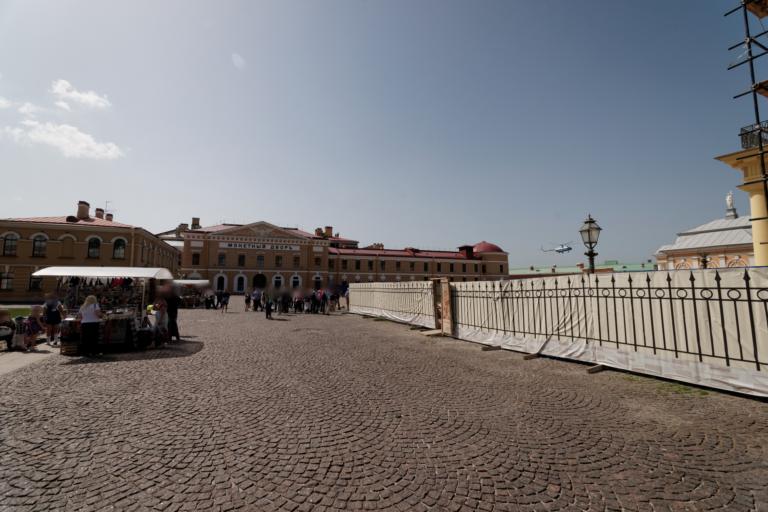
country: RU
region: St.-Petersburg
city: Saint Petersburg
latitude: 59.9498
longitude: 30.3161
